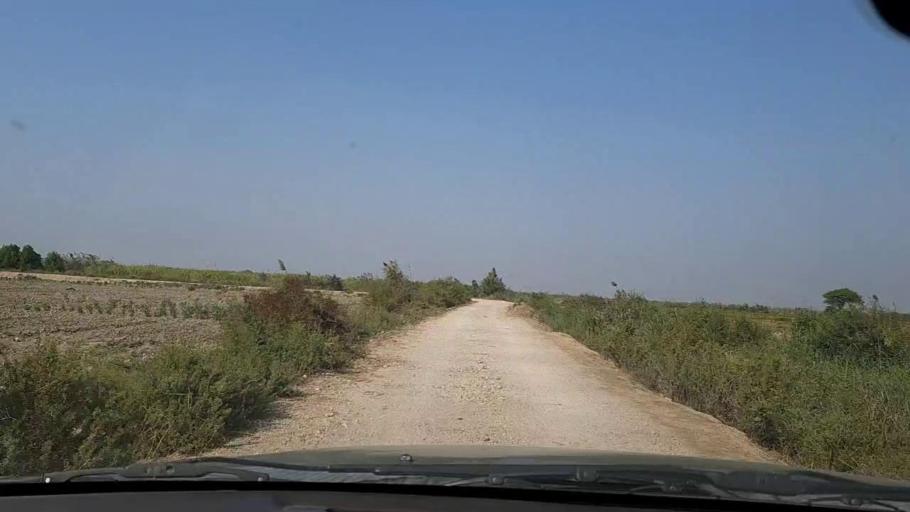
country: PK
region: Sindh
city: Mirpur Sakro
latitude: 24.3760
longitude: 67.6829
